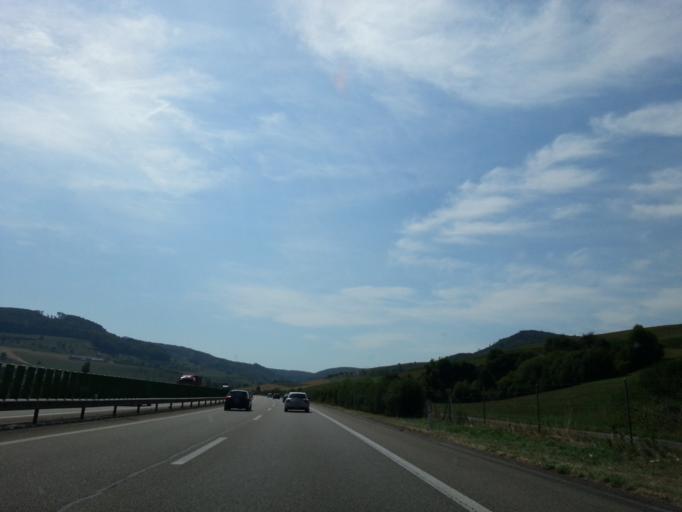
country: CH
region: Basel-Landschaft
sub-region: Bezirk Liestal
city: Arisdorf
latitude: 47.5189
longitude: 7.7539
